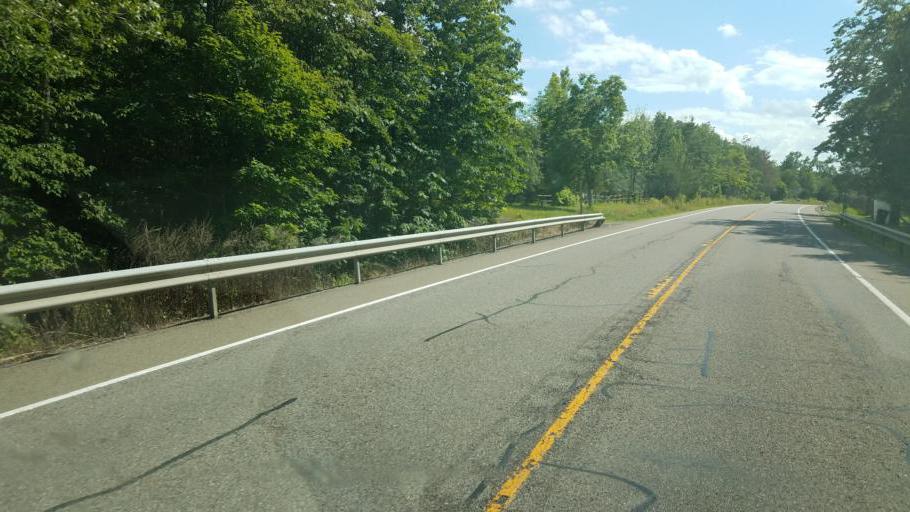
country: US
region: New York
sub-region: Steuben County
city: Sylvan Beach
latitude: 42.4785
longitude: -77.1478
